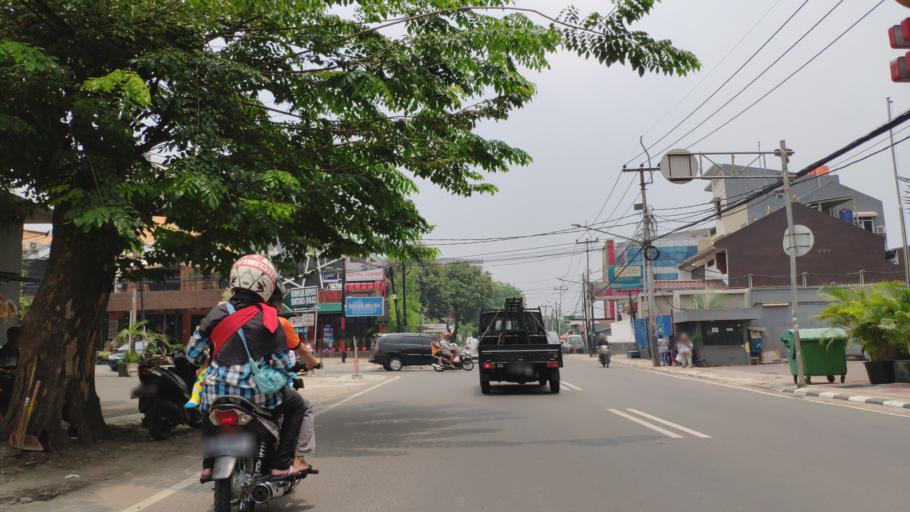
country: ID
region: Banten
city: South Tangerang
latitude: -6.2638
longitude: 106.7663
